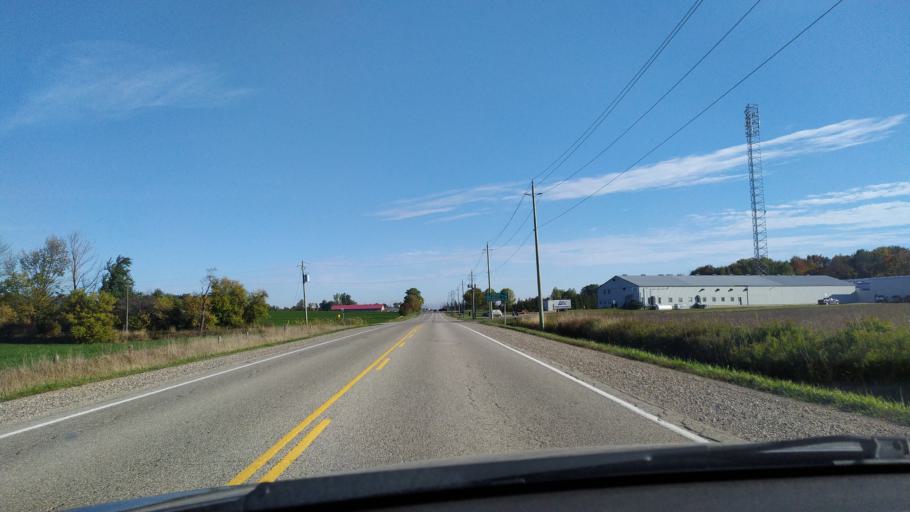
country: CA
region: Ontario
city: Stratford
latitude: 43.4755
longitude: -80.7822
